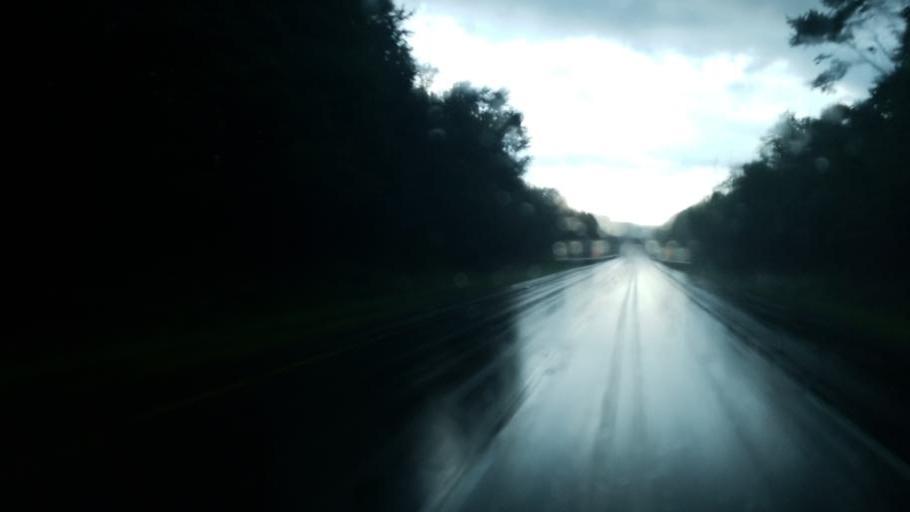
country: US
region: Pennsylvania
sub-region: Butler County
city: Prospect
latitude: 40.8899
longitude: -80.1205
